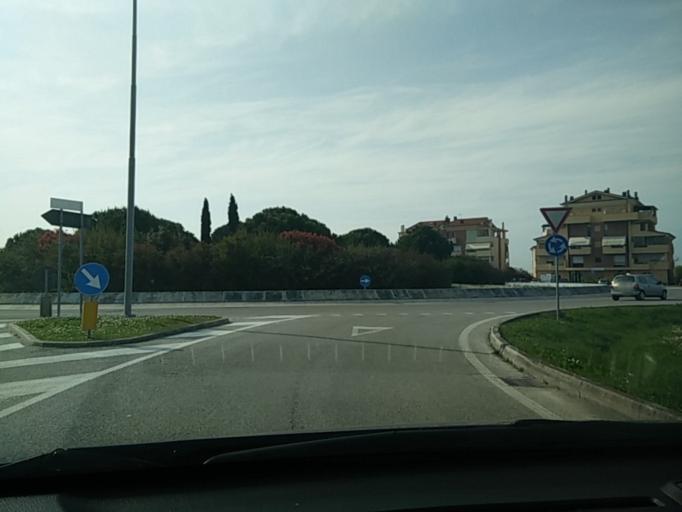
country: IT
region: Emilia-Romagna
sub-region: Provincia di Rimini
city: Santa Giustina
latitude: 44.0721
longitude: 12.5157
